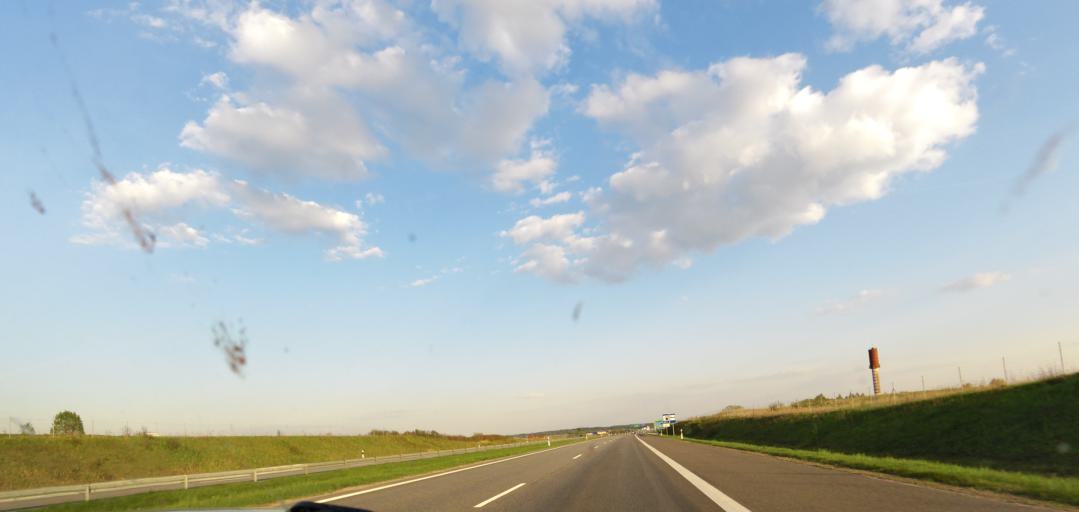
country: LT
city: Grigiskes
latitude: 54.8803
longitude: 25.0673
